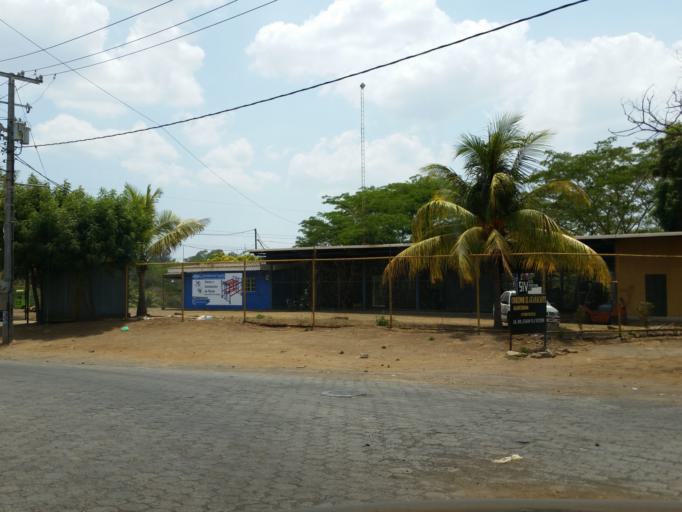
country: NI
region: Managua
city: Managua
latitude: 12.0921
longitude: -86.2346
